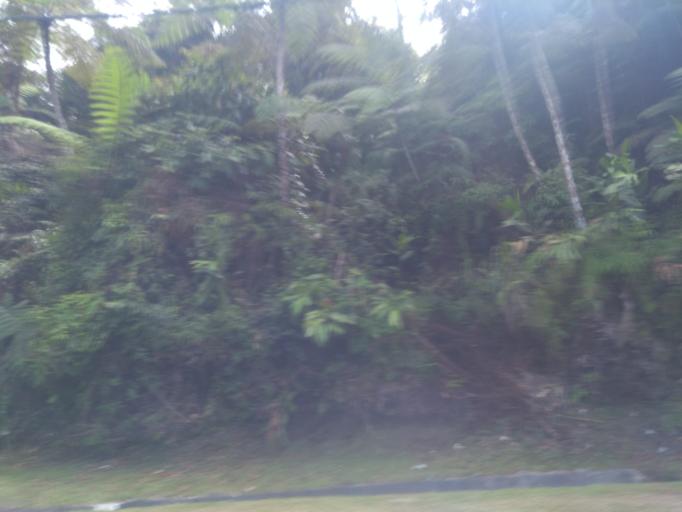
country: MY
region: Pahang
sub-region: Cameron Highlands
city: Tanah Rata
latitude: 4.4664
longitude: 101.3670
